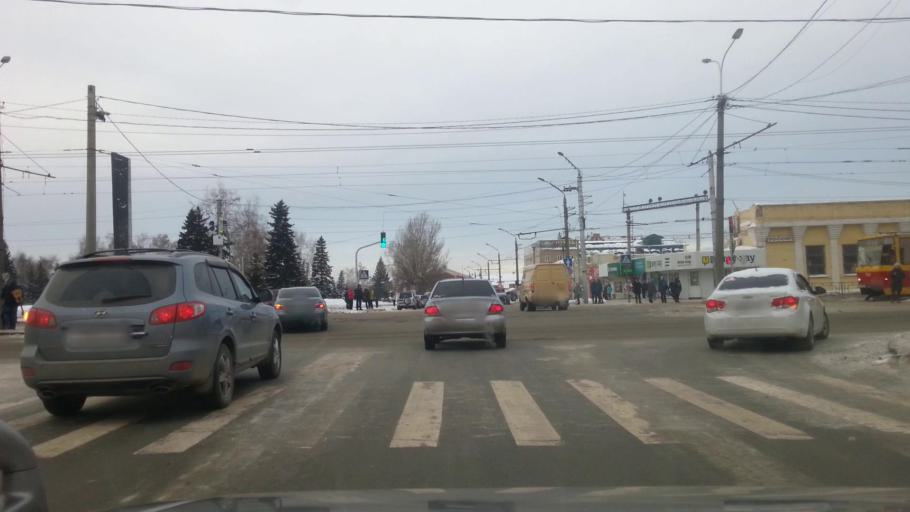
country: RU
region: Altai Krai
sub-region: Gorod Barnaulskiy
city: Barnaul
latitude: 53.3498
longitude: 83.7626
